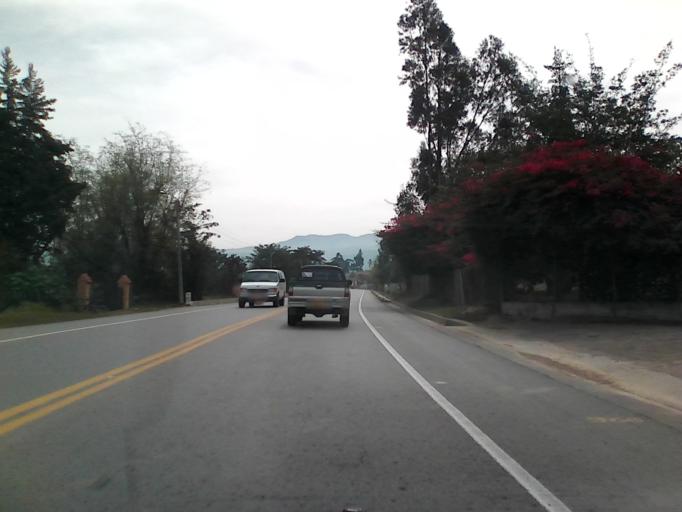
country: CO
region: Boyaca
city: Tibasosa
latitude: 5.7444
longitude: -72.9856
